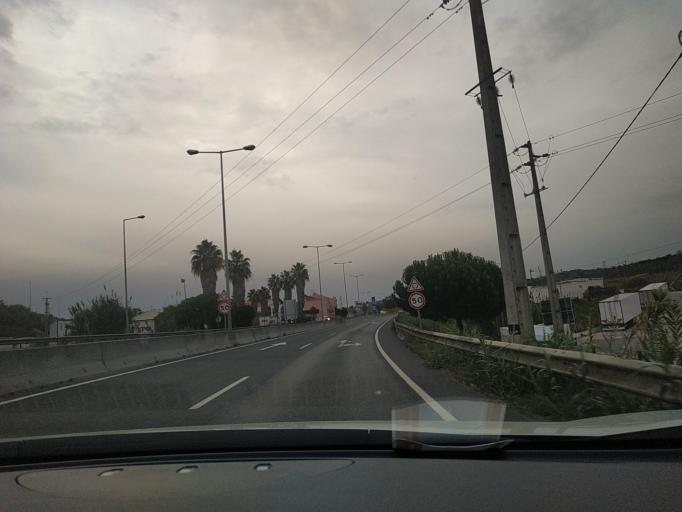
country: PT
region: Lisbon
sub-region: Loures
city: Santa Iria da Azoia
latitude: 38.8633
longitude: -9.1050
